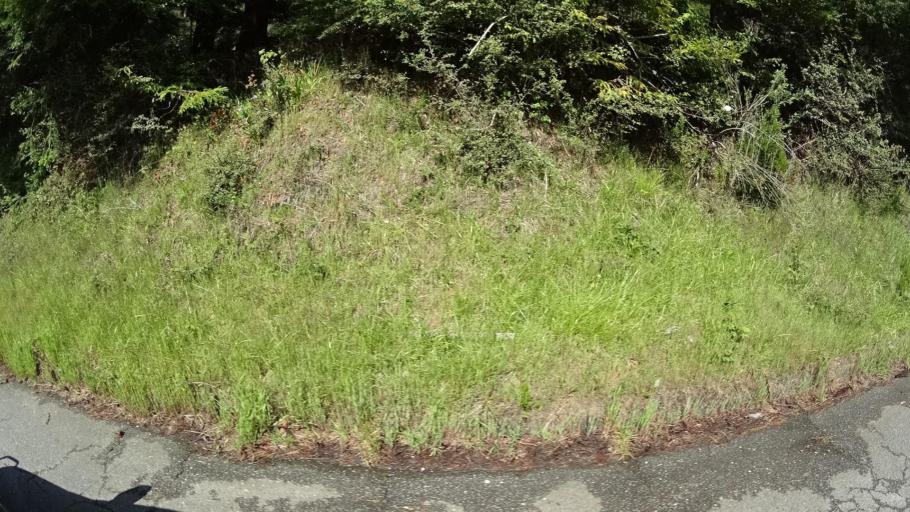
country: US
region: California
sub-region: Humboldt County
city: Hydesville
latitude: 40.5695
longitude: -124.1210
